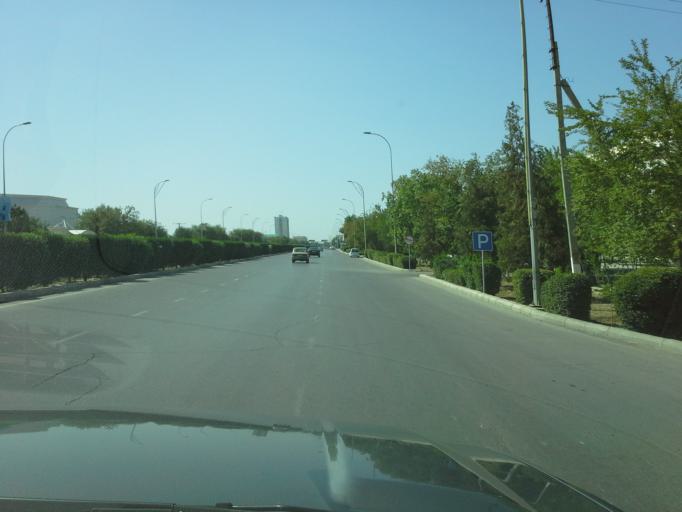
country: TM
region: Dasoguz
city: Dasoguz
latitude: 41.8335
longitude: 59.9695
